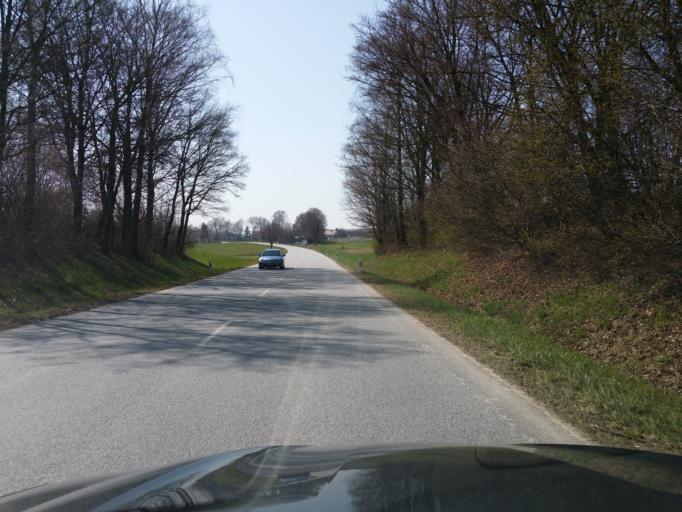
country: DE
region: Bavaria
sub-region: Lower Bavaria
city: Altfraunhofen
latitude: 48.4617
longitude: 12.1505
